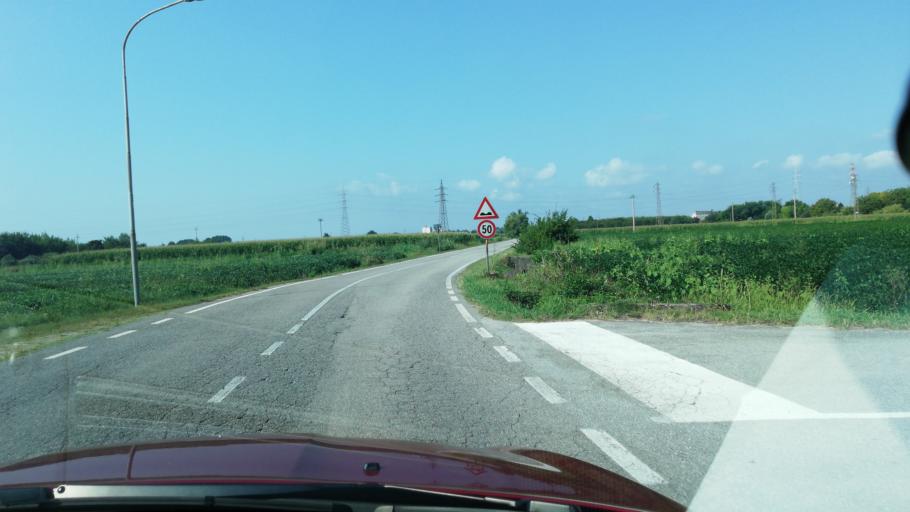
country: IT
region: Friuli Venezia Giulia
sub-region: Provincia di Udine
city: Latisana
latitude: 45.7873
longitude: 13.0197
